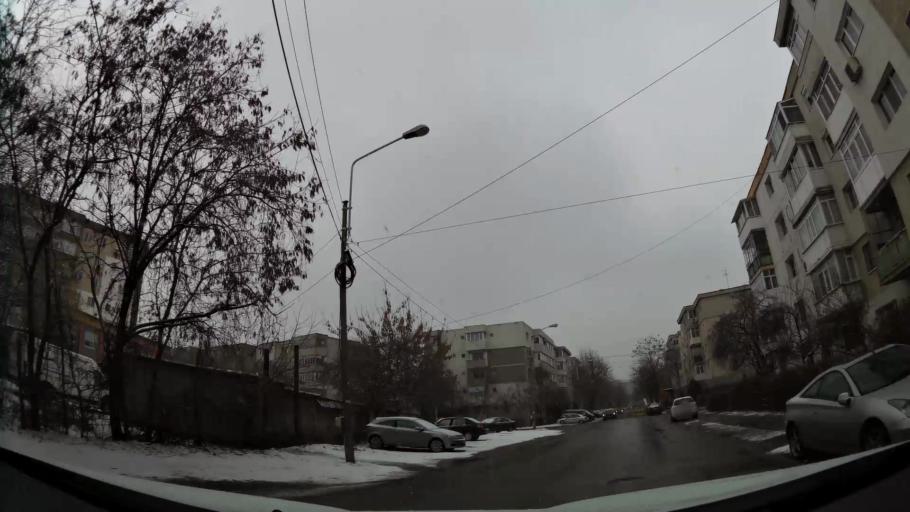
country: RO
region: Prahova
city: Ploiesti
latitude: 44.9279
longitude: 26.0018
